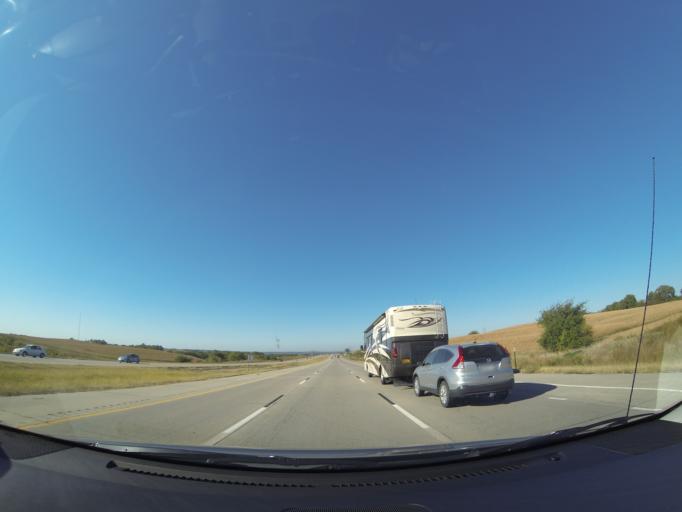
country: US
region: Nebraska
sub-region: Sarpy County
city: Gretna
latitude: 41.0913
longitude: -96.2602
